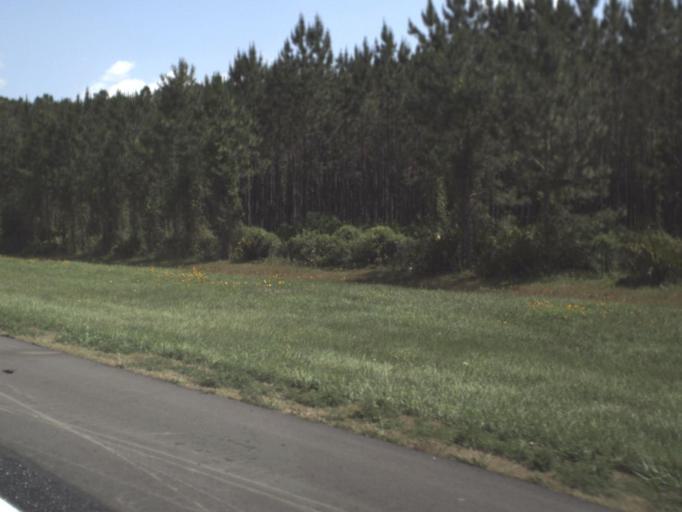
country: US
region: Florida
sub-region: Nassau County
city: Yulee
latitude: 30.6404
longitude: -81.6572
